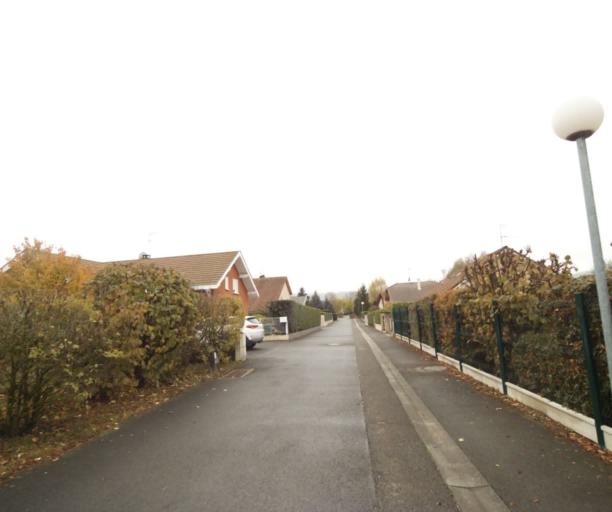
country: FR
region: Rhone-Alpes
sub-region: Departement de la Haute-Savoie
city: Reignier-Esery
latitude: 46.1353
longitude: 6.2839
